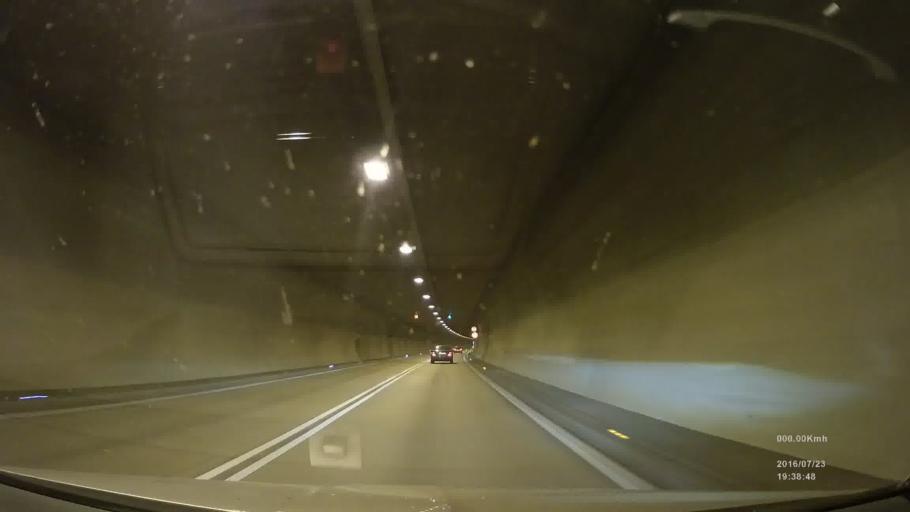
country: SK
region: Kosicky
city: Krompachy
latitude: 49.0091
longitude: 20.8522
